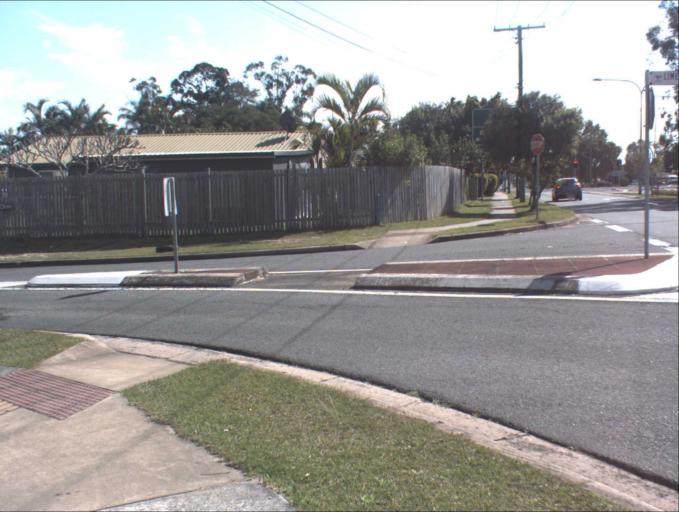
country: AU
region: Queensland
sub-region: Logan
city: Logan Reserve
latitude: -27.6818
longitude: 153.0885
